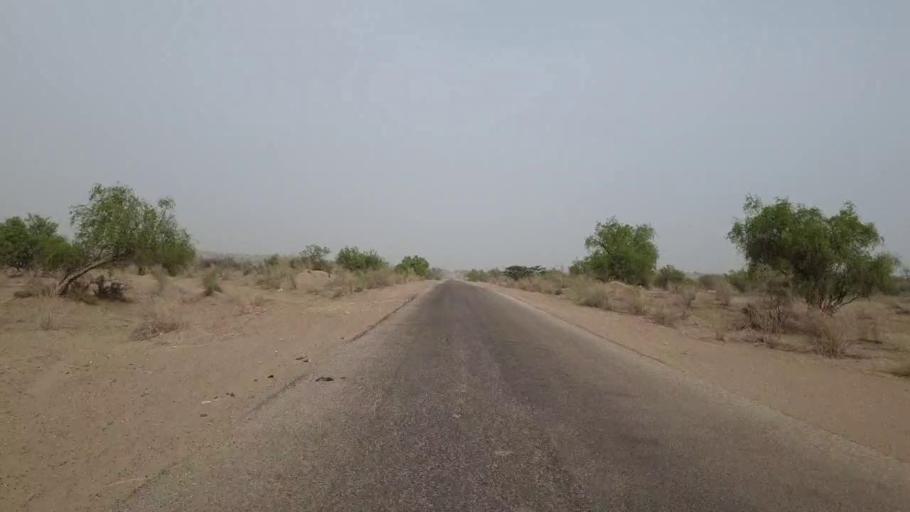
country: PK
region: Sindh
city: Islamkot
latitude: 24.5670
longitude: 70.3287
